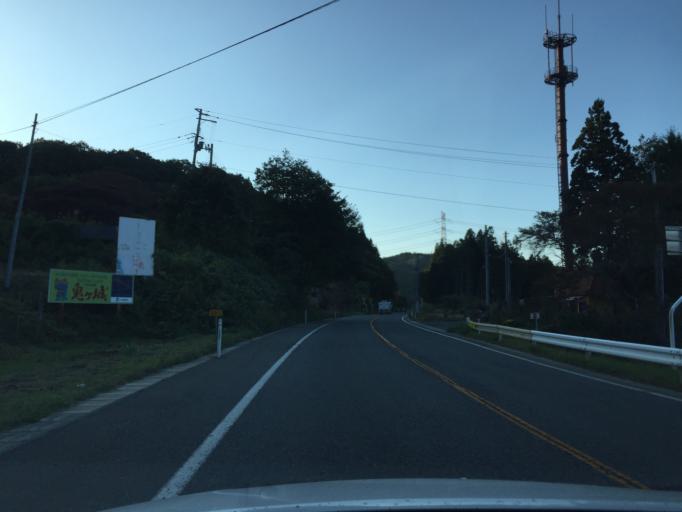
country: JP
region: Fukushima
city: Ishikawa
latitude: 37.1926
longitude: 140.6331
